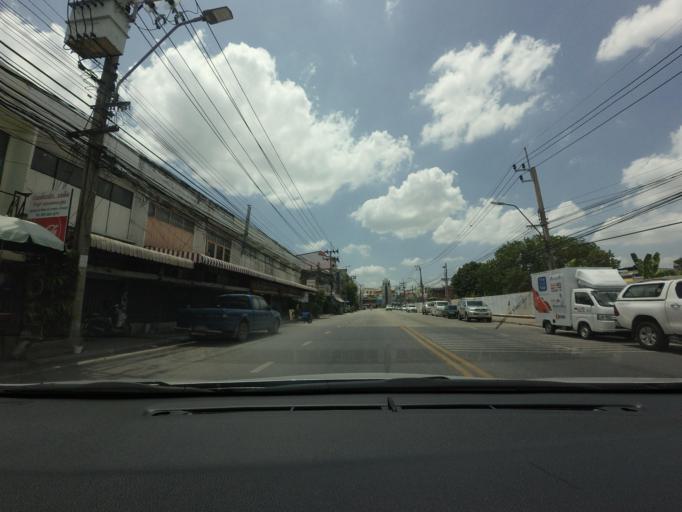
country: TH
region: Samut Prakan
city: Samut Prakan
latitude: 13.5894
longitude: 100.5962
